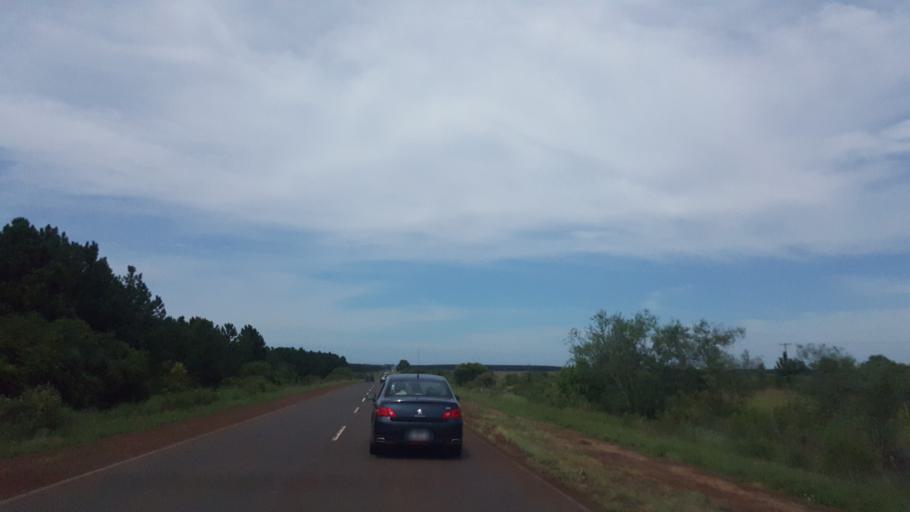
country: PY
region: Itapua
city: San Juan del Parana
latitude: -27.5070
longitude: -56.1278
